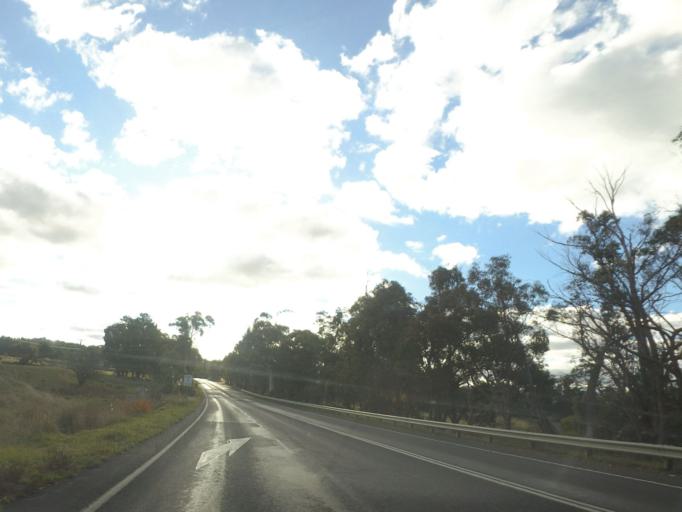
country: AU
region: Victoria
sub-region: Mount Alexander
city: Castlemaine
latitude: -37.1243
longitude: 144.3440
